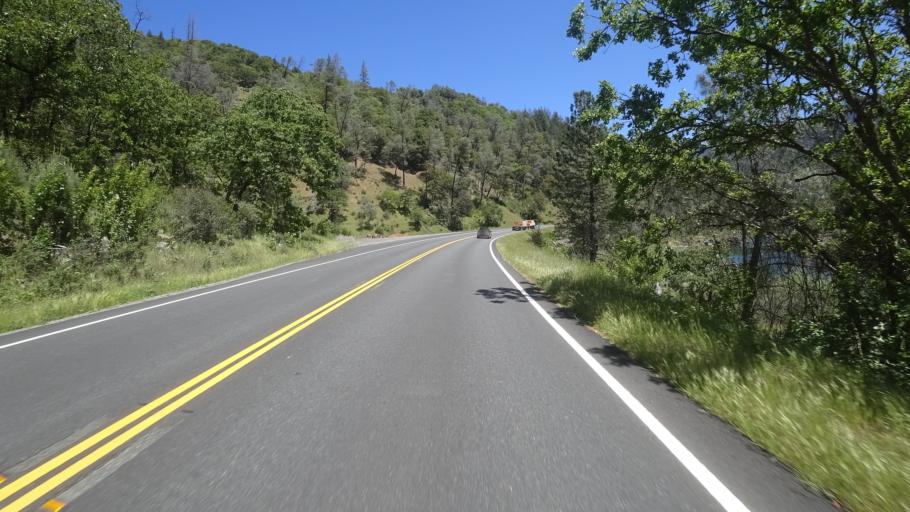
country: US
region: California
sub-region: Humboldt County
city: Willow Creek
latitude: 40.7907
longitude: -123.4372
